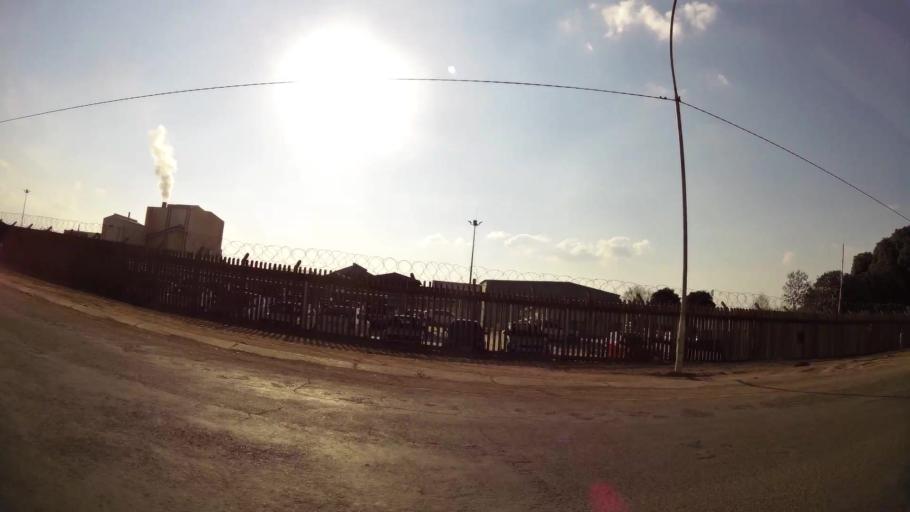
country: ZA
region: Gauteng
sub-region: Ekurhuleni Metropolitan Municipality
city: Tembisa
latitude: -25.9451
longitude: 28.2275
